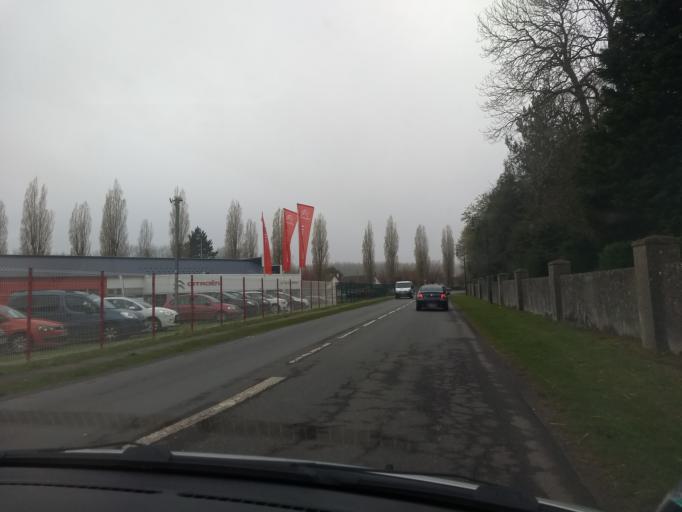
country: FR
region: Nord-Pas-de-Calais
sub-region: Departement du Pas-de-Calais
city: Verton
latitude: 50.4050
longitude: 1.6489
